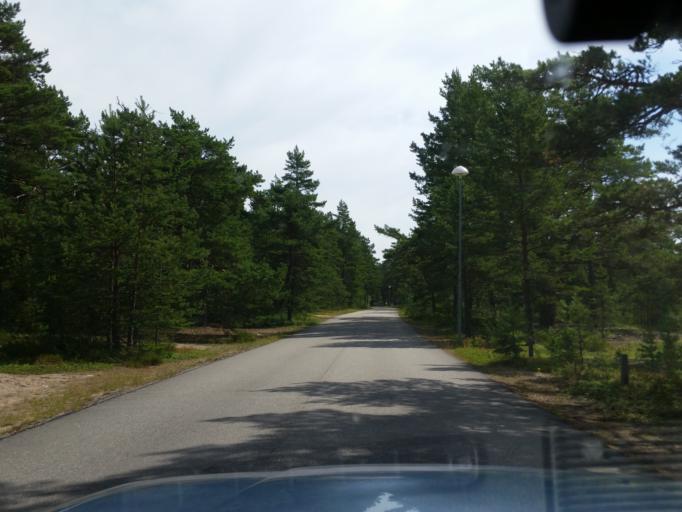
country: FI
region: Uusimaa
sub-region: Raaseporin
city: Hanko
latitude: 59.8275
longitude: 23.0048
